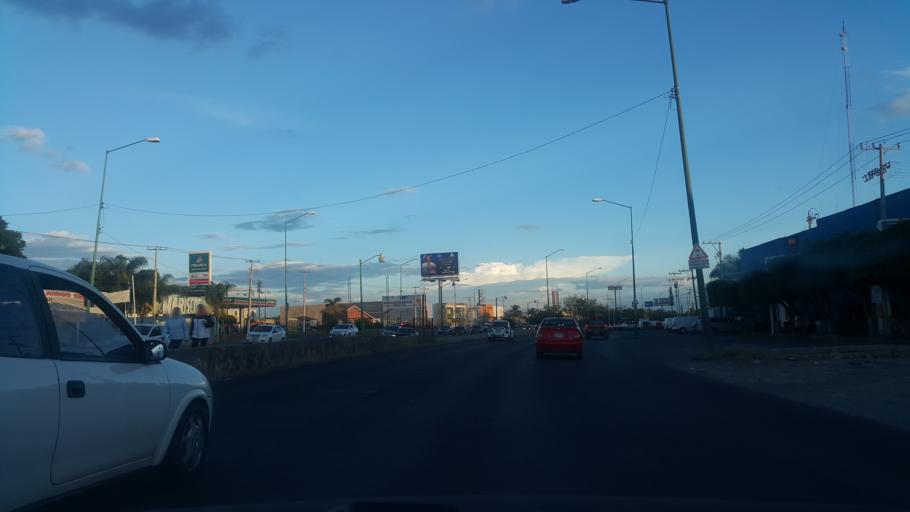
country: MX
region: Guanajuato
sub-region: Leon
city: Medina
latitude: 21.1517
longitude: -101.6361
